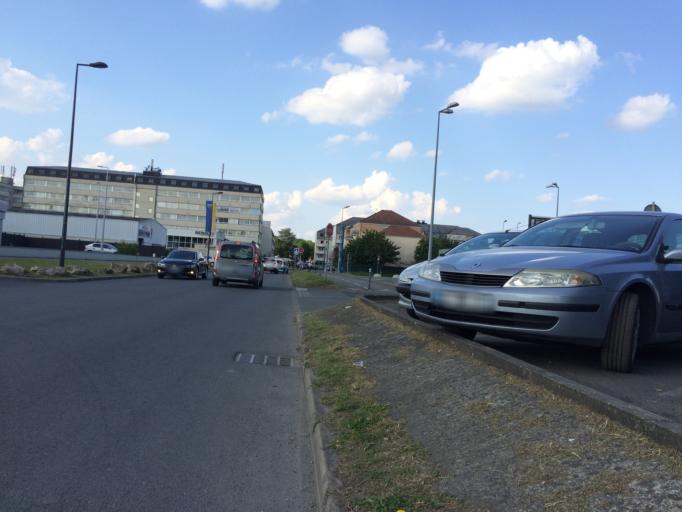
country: FR
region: Ile-de-France
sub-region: Departement de l'Essonne
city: Grigny
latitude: 48.6499
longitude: 2.3986
